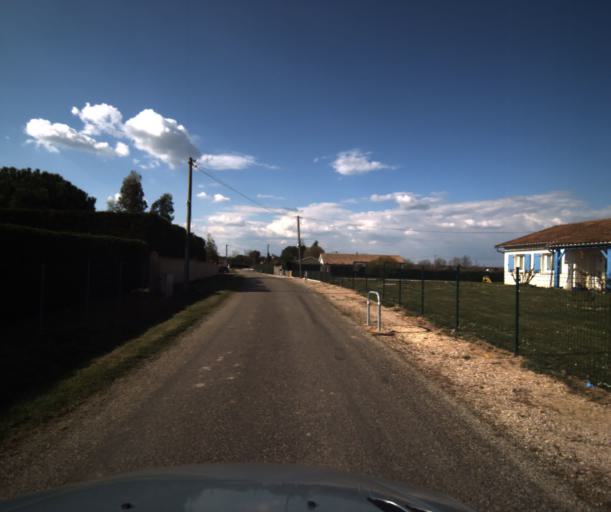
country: FR
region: Midi-Pyrenees
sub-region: Departement du Tarn-et-Garonne
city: Bressols
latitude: 43.9622
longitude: 1.3048
